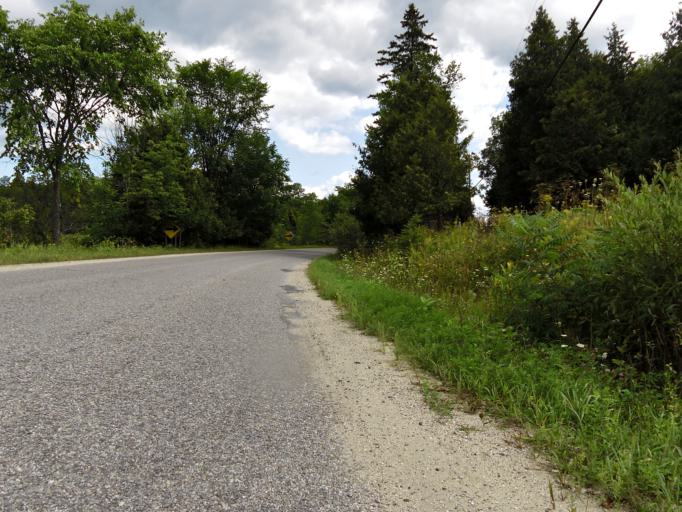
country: CA
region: Quebec
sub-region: Outaouais
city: Wakefield
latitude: 45.8089
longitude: -76.0051
